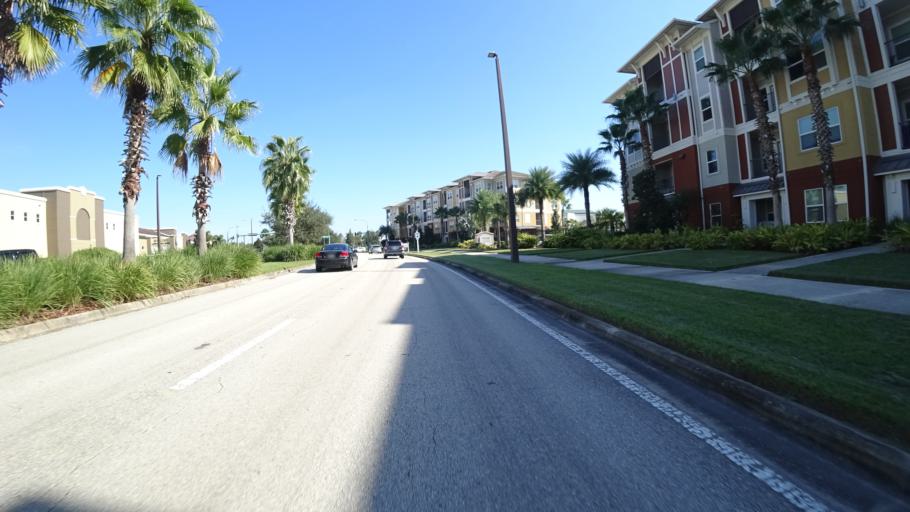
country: US
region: Florida
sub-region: Sarasota County
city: The Meadows
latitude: 27.3933
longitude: -82.4371
